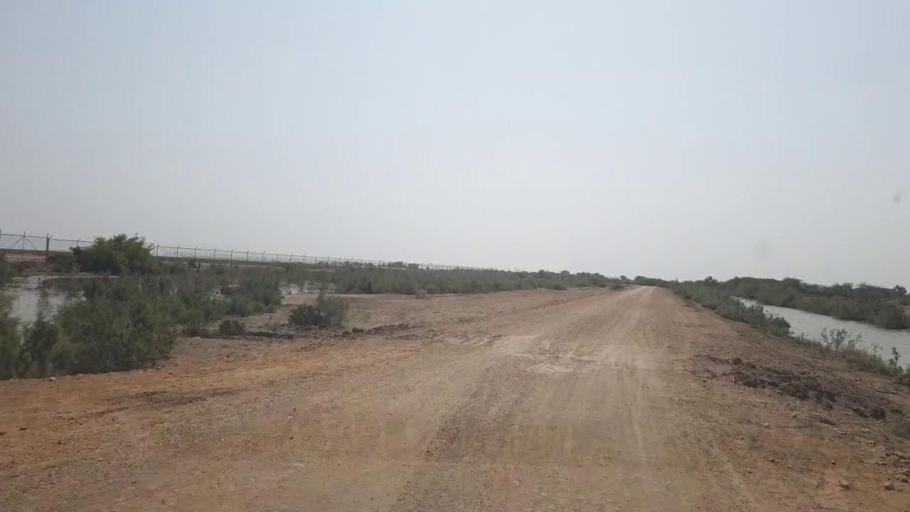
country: PK
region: Sindh
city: Jati
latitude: 24.3871
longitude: 68.5985
